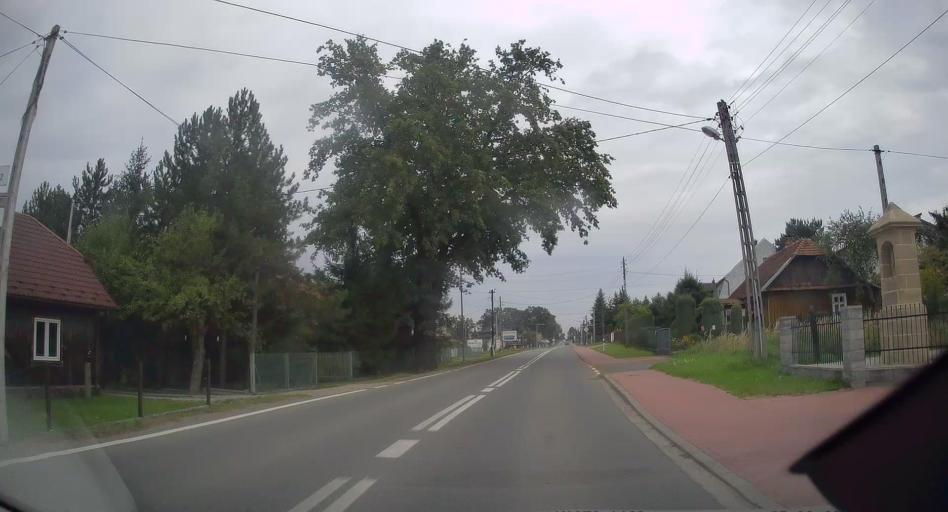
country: PL
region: Lesser Poland Voivodeship
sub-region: Powiat wielicki
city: Niepolomice
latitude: 50.0259
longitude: 20.2011
